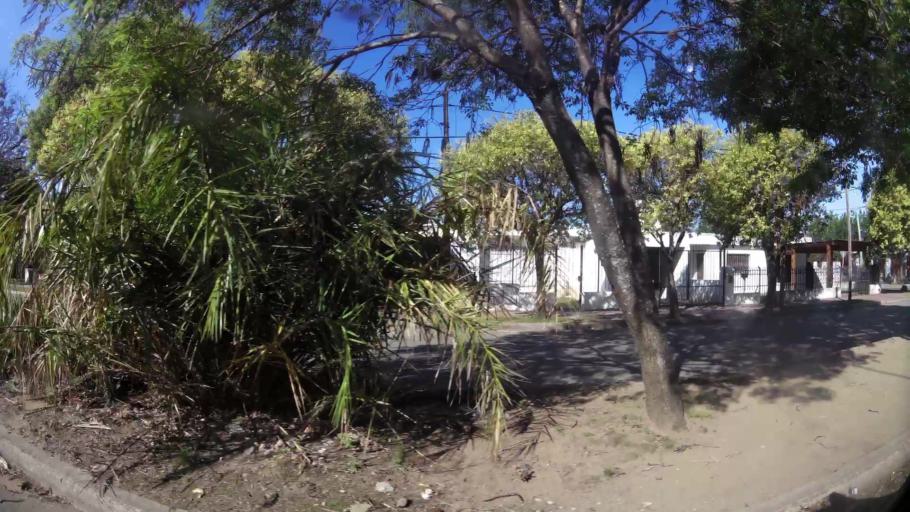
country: AR
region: Cordoba
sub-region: Departamento de Capital
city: Cordoba
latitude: -31.3626
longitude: -64.1923
